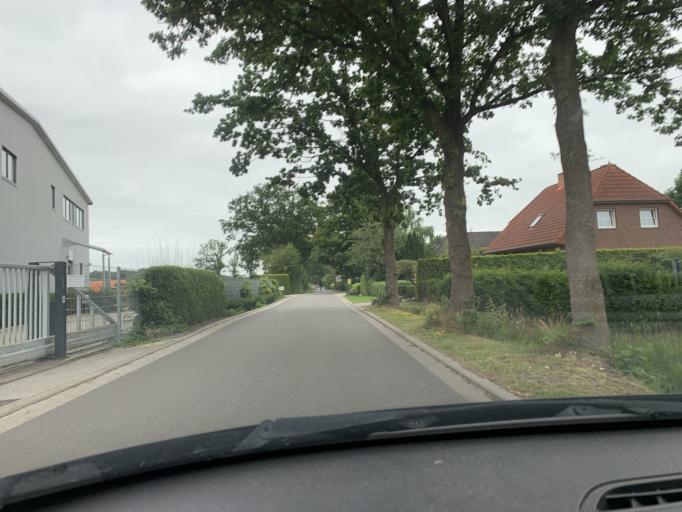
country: DE
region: Lower Saxony
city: Westerstede
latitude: 53.2449
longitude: 7.9049
